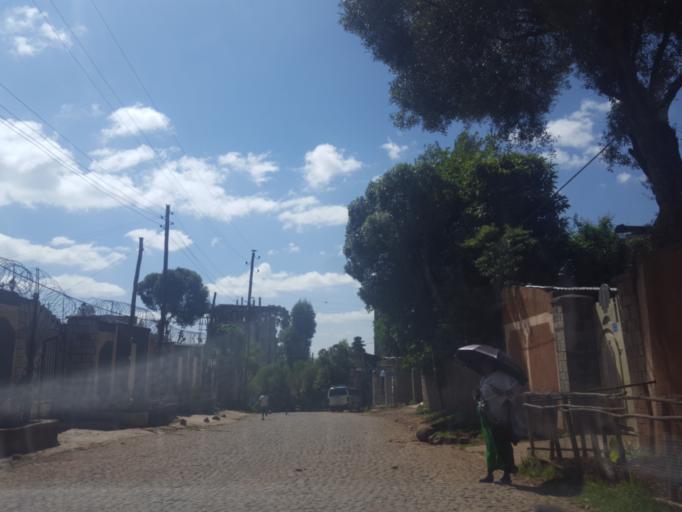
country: ET
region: Adis Abeba
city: Addis Ababa
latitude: 9.0608
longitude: 38.7411
